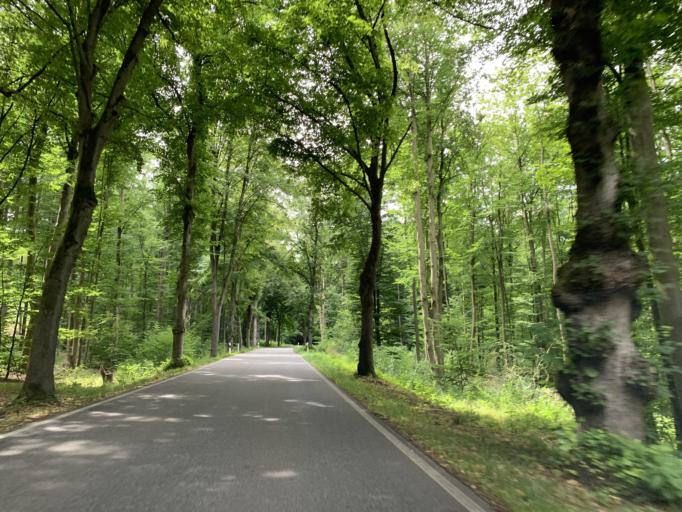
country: DE
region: Mecklenburg-Vorpommern
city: Burg Stargard
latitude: 53.4851
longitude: 13.3003
